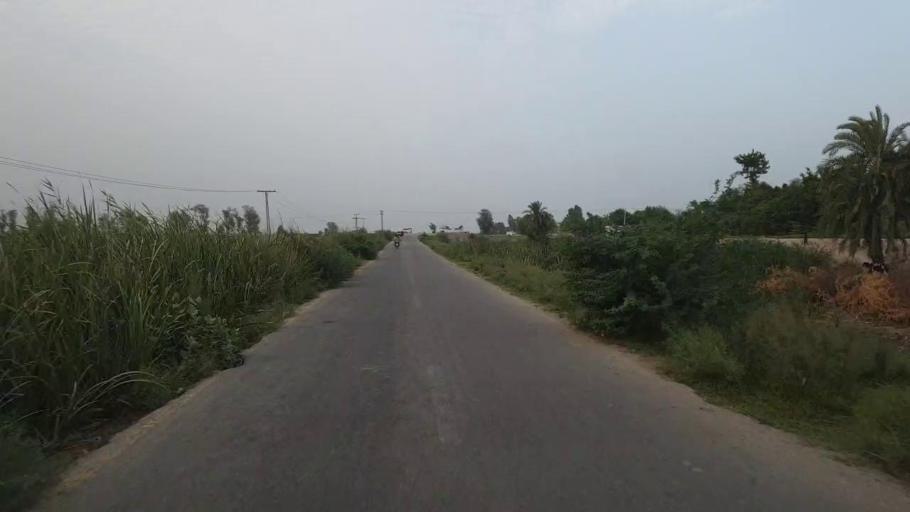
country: PK
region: Sindh
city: Daur
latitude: 26.4554
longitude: 68.2936
